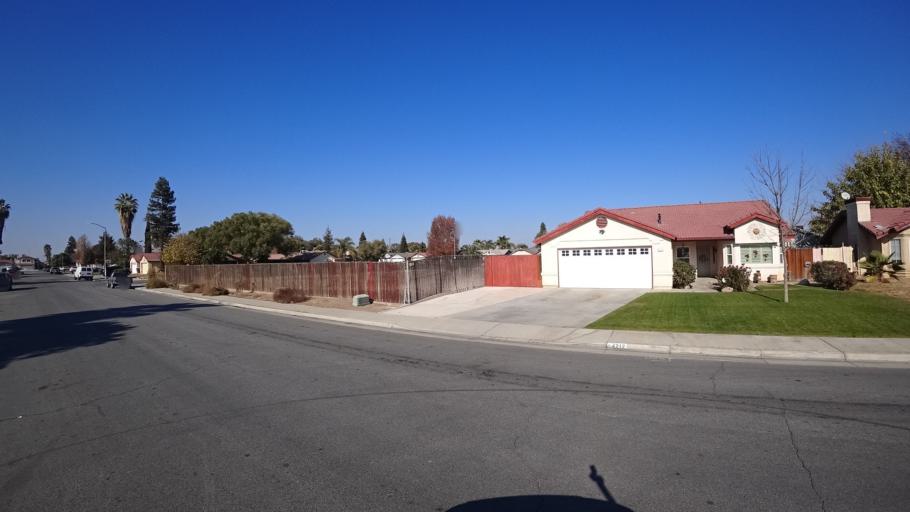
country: US
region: California
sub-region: Kern County
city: Greenfield
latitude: 35.2937
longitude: -119.0498
